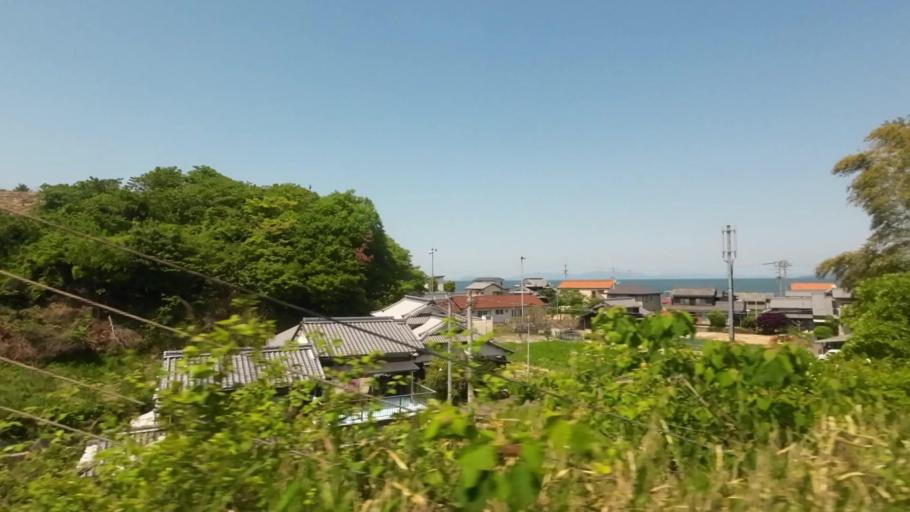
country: JP
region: Ehime
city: Hojo
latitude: 33.9995
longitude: 132.7754
